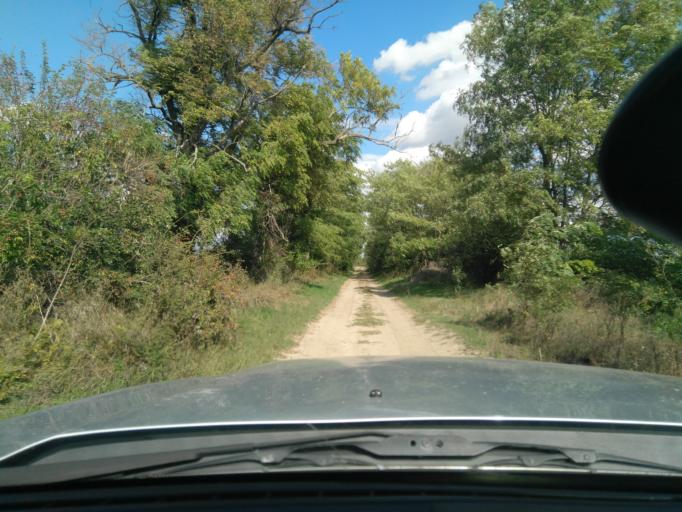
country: HU
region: Fejer
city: Bicske
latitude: 47.4511
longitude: 18.6639
